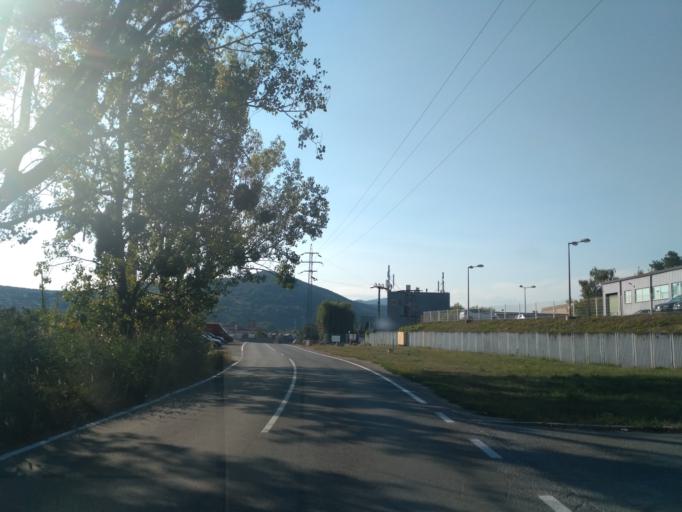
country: SK
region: Kosicky
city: Kosice
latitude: 48.7485
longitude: 21.2665
